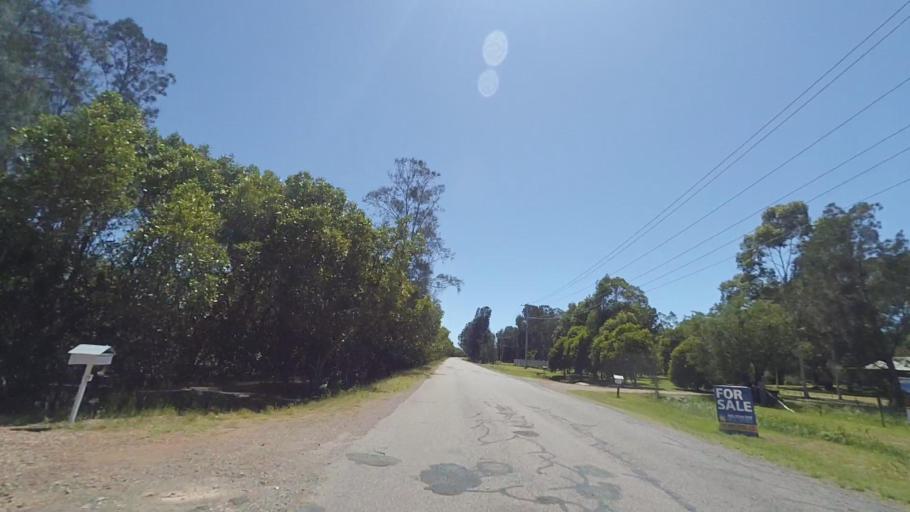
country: AU
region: New South Wales
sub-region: Port Stephens Shire
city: Medowie
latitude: -32.7837
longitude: 151.9409
